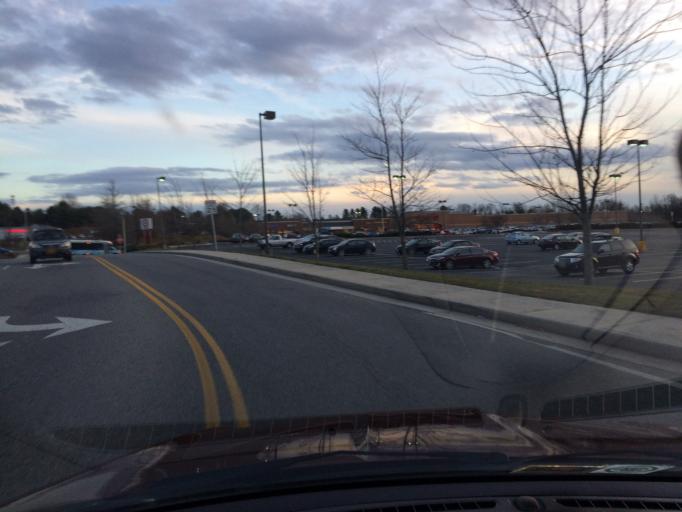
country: US
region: Virginia
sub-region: Montgomery County
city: Merrimac
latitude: 37.1596
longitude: -80.4226
